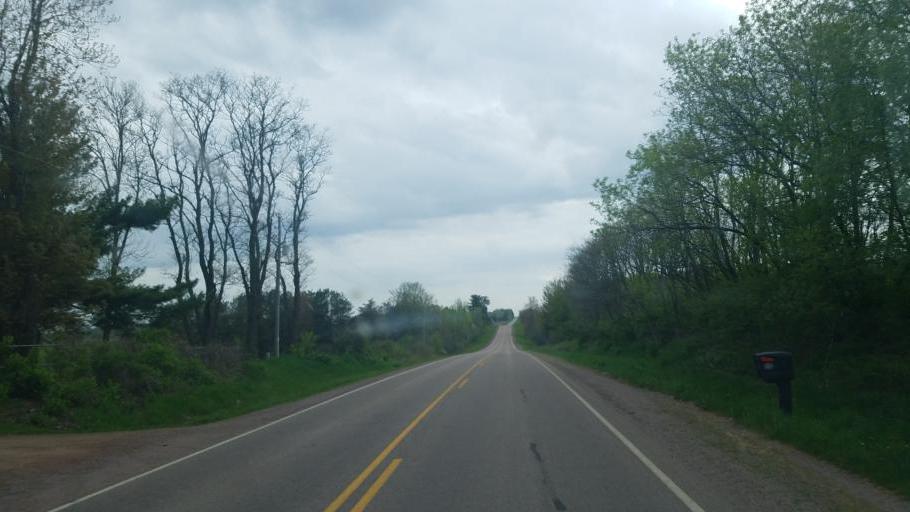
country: US
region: Wisconsin
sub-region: Wood County
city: Marshfield
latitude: 44.5746
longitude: -90.2996
